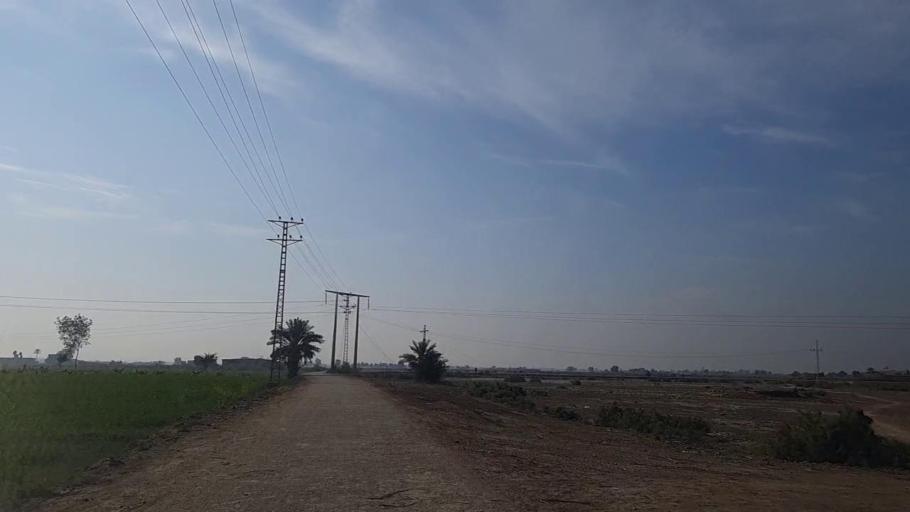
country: PK
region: Sindh
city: Mirpur Khas
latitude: 25.5015
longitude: 69.0000
